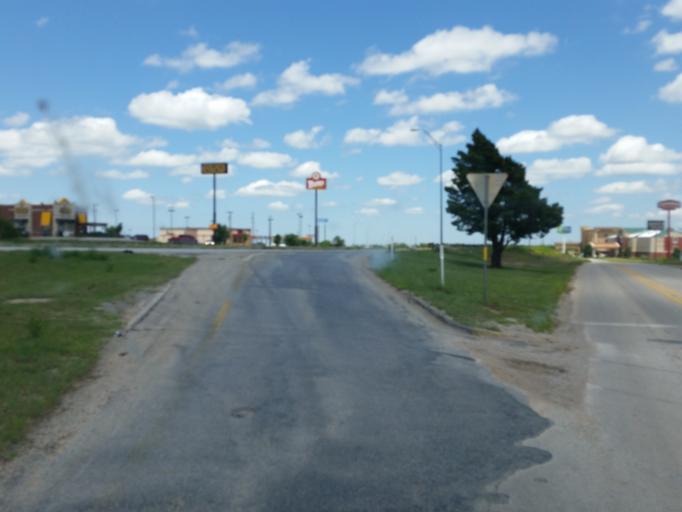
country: US
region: Texas
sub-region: Nolan County
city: Sweetwater
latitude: 32.4502
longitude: -100.3962
